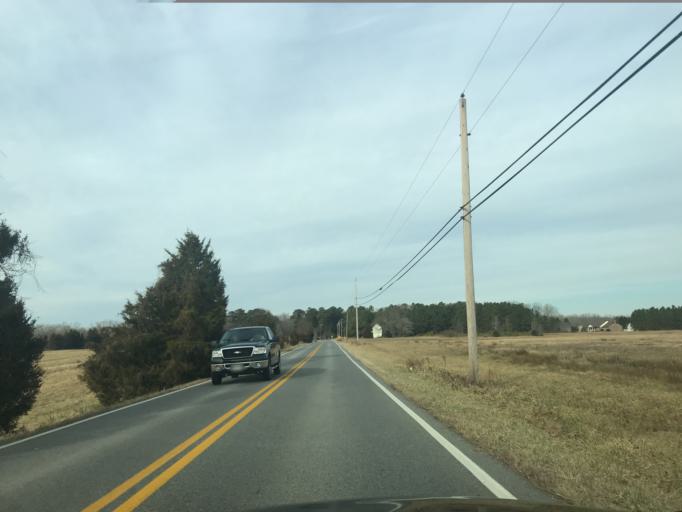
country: US
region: Maryland
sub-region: Saint Mary's County
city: Charlotte Hall
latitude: 38.4938
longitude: -76.8794
